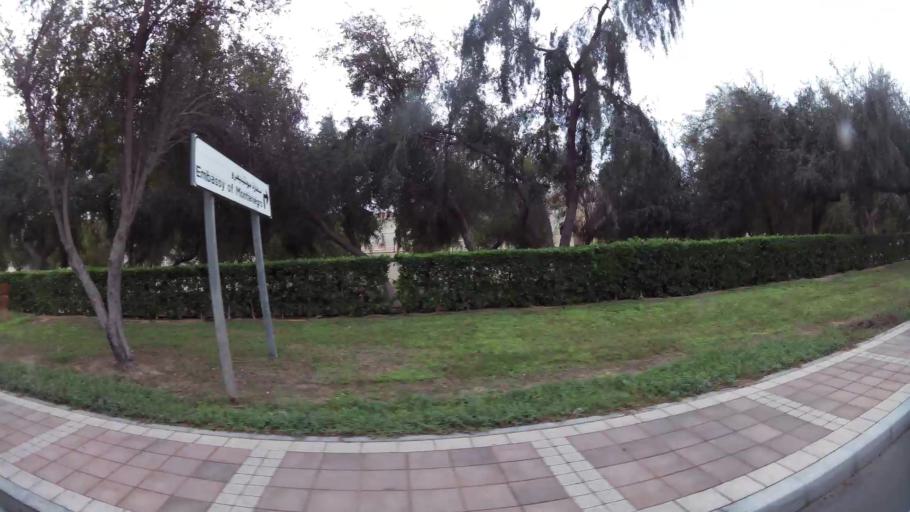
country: AE
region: Abu Dhabi
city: Abu Dhabi
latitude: 24.4286
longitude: 54.4274
